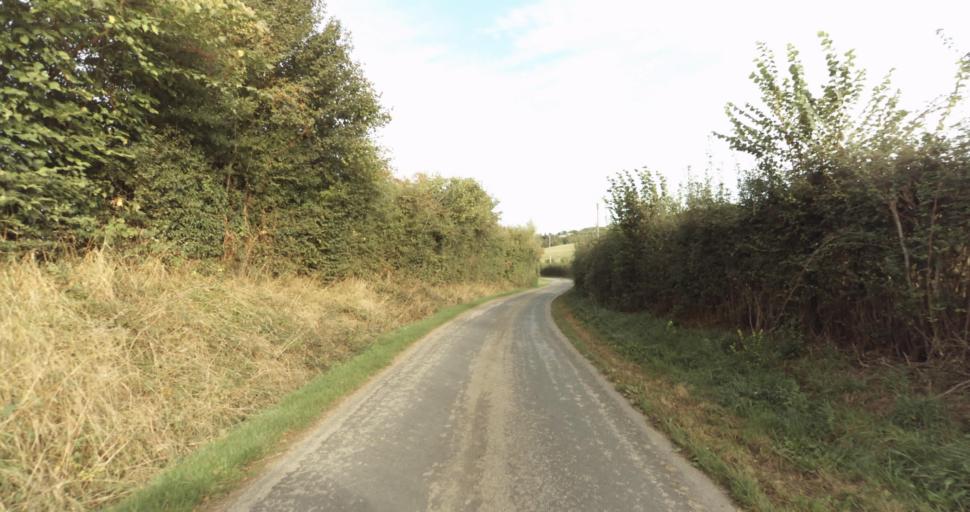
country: FR
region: Lower Normandy
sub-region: Departement de l'Orne
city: Vimoutiers
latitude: 48.8716
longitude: 0.2408
